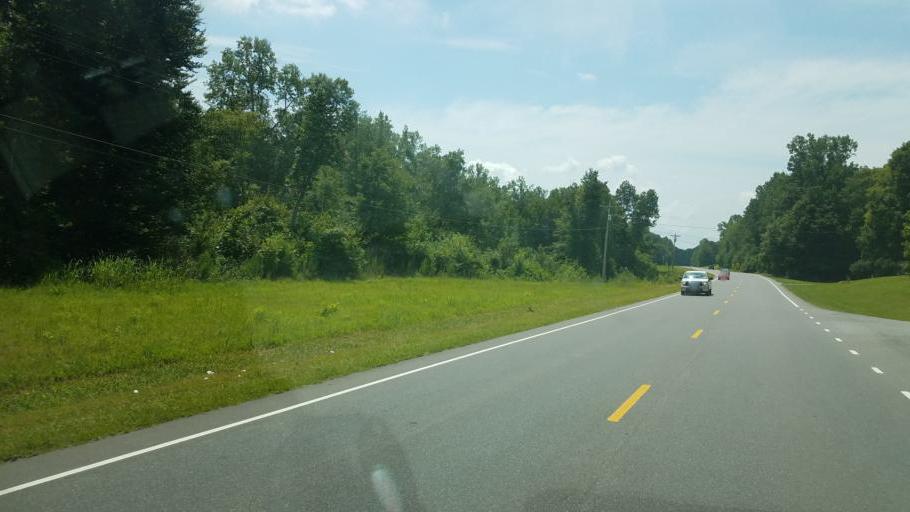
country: US
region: North Carolina
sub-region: Cleveland County
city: Kings Mountain
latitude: 35.2028
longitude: -81.3412
